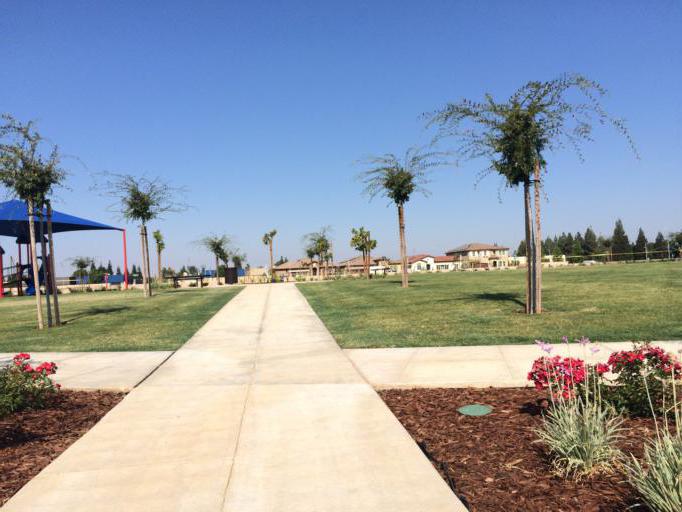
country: US
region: California
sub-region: Fresno County
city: Tarpey Village
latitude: 36.7740
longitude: -119.6800
